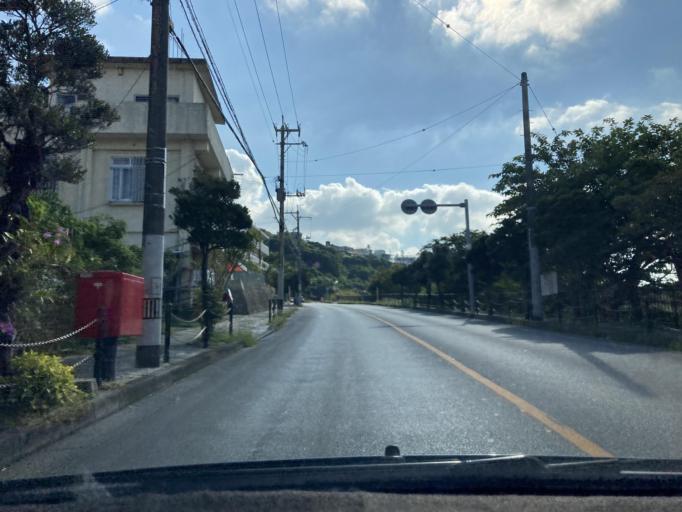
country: JP
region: Okinawa
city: Naha-shi
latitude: 26.2133
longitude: 127.7171
